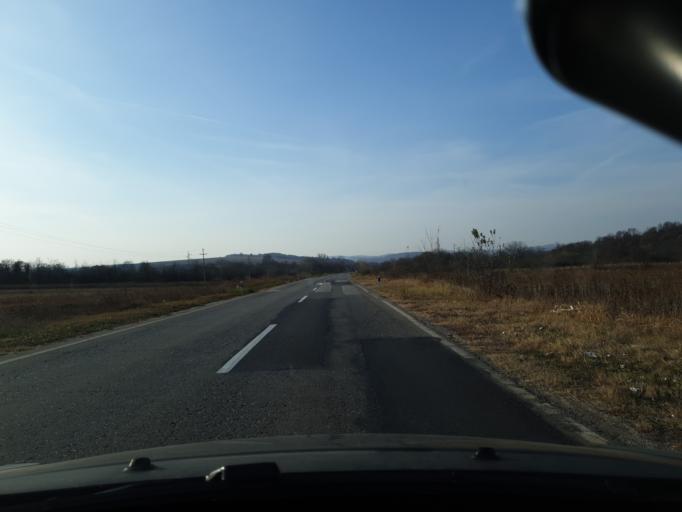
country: RS
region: Central Serbia
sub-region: Zajecarski Okrug
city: Zajecar
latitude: 43.9486
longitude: 22.2933
